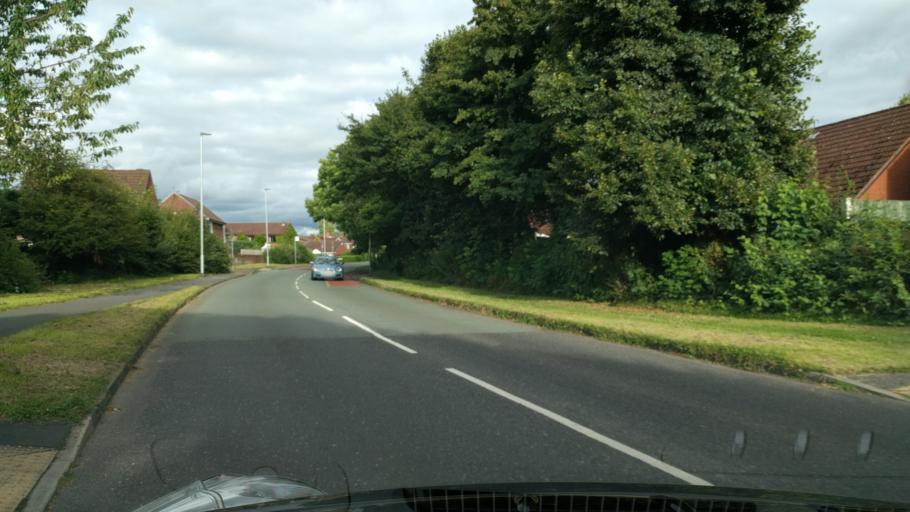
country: GB
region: England
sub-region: Warrington
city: Croft
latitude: 53.4181
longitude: -2.5559
